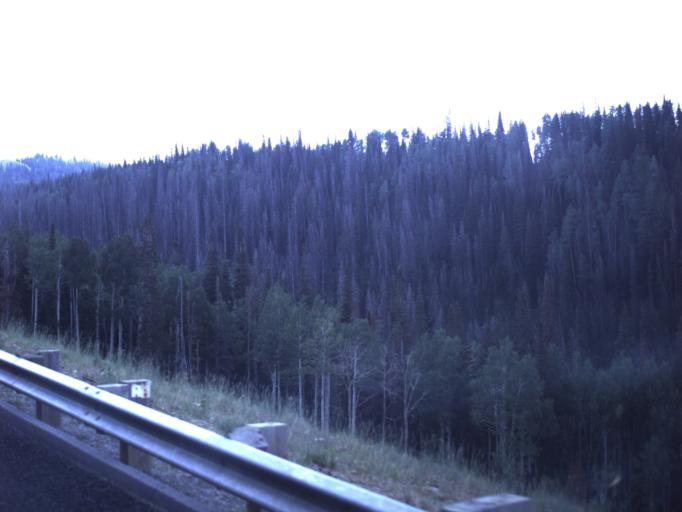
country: US
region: Utah
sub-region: Summit County
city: Francis
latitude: 40.5045
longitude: -111.0444
